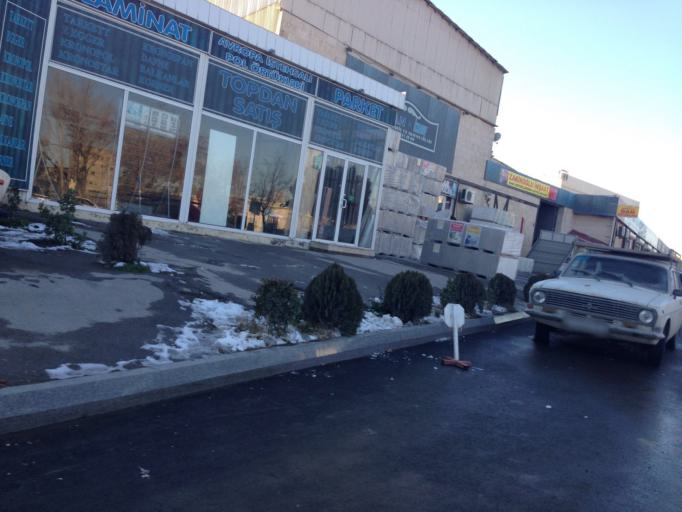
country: AZ
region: Baki
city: Baku
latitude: 40.4183
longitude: 49.8566
